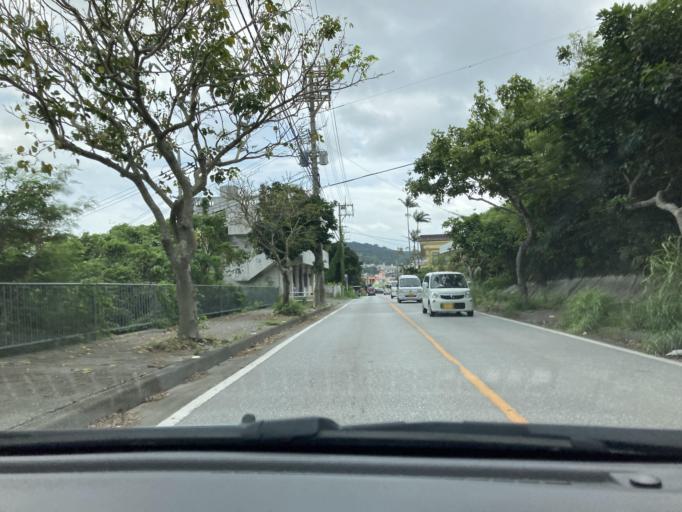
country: JP
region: Okinawa
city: Chatan
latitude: 26.2879
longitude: 127.7865
